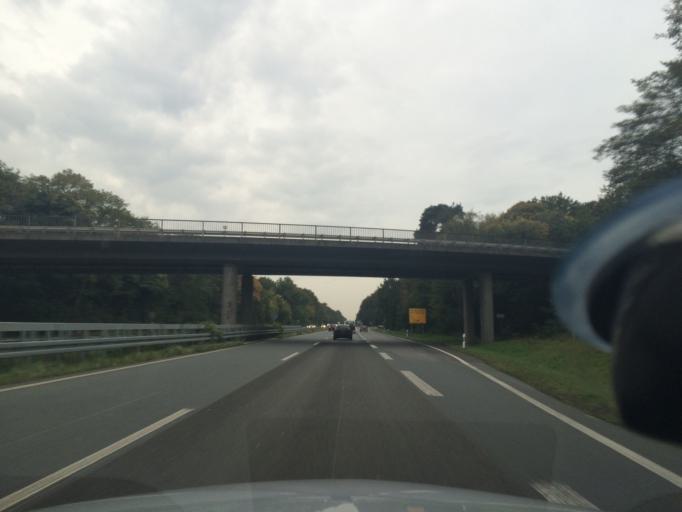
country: DE
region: Hesse
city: Niederrad
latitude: 50.0502
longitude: 8.6423
